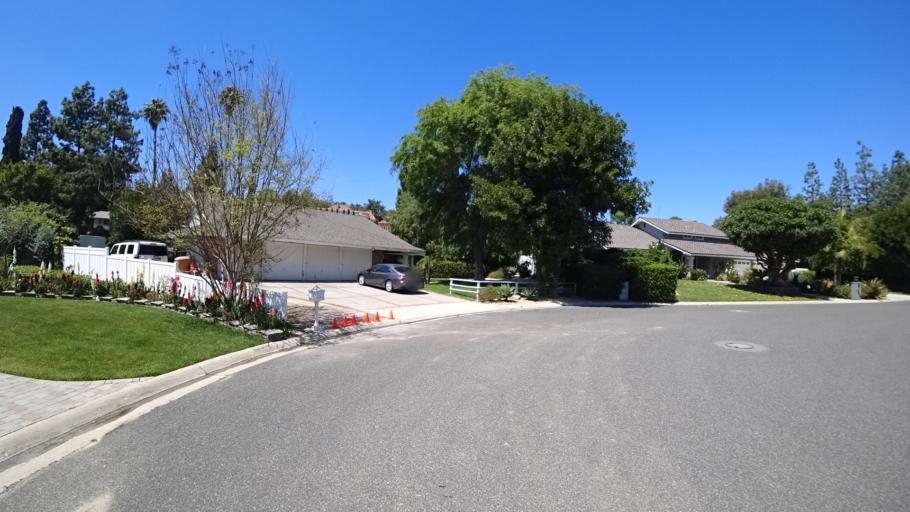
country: US
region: California
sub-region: Orange County
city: Villa Park
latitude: 33.8242
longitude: -117.8078
